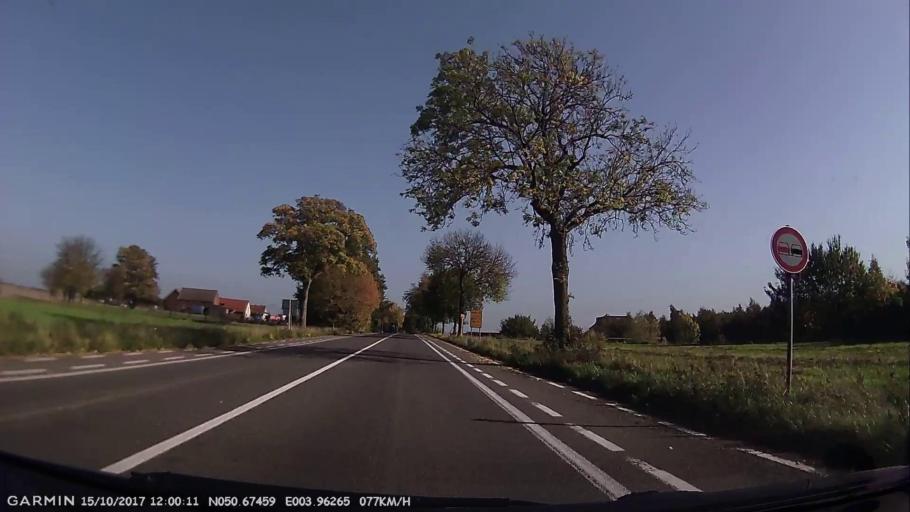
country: BE
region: Wallonia
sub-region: Province du Hainaut
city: Silly
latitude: 50.6747
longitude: 3.9630
